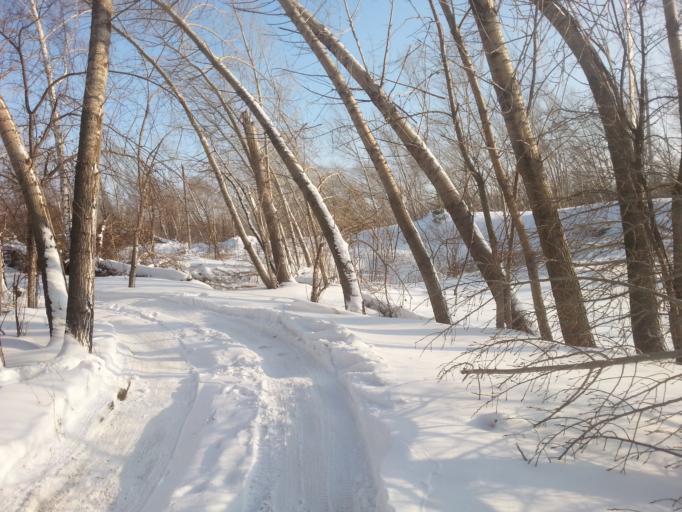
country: RU
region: Altai Krai
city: Zaton
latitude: 53.3176
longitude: 83.8070
